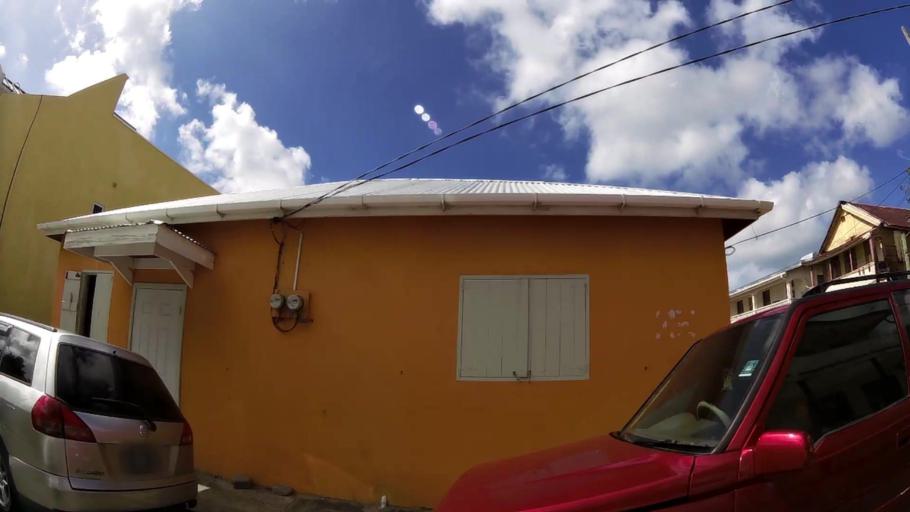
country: LC
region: Laborie Quarter
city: Laborie
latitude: 13.7512
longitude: -60.9954
